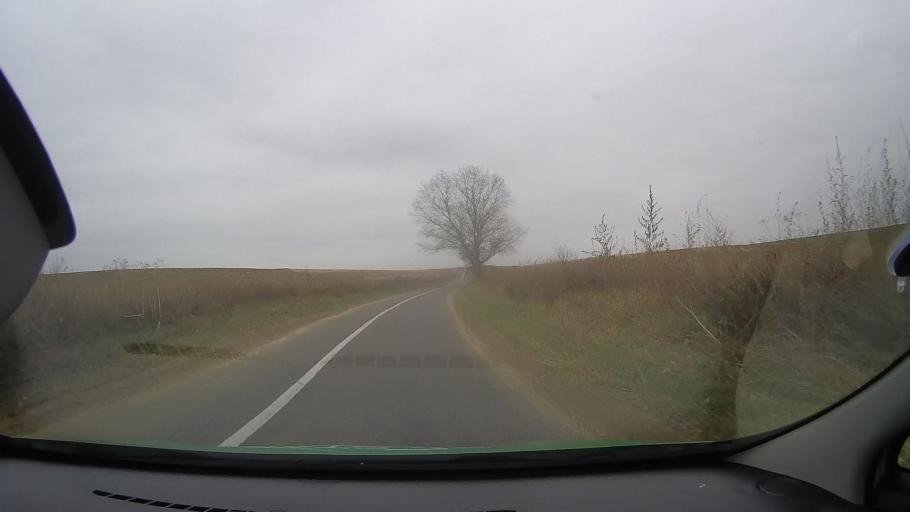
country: RO
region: Constanta
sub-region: Comuna Saraiu
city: Saraiu
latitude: 44.7247
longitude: 28.1856
